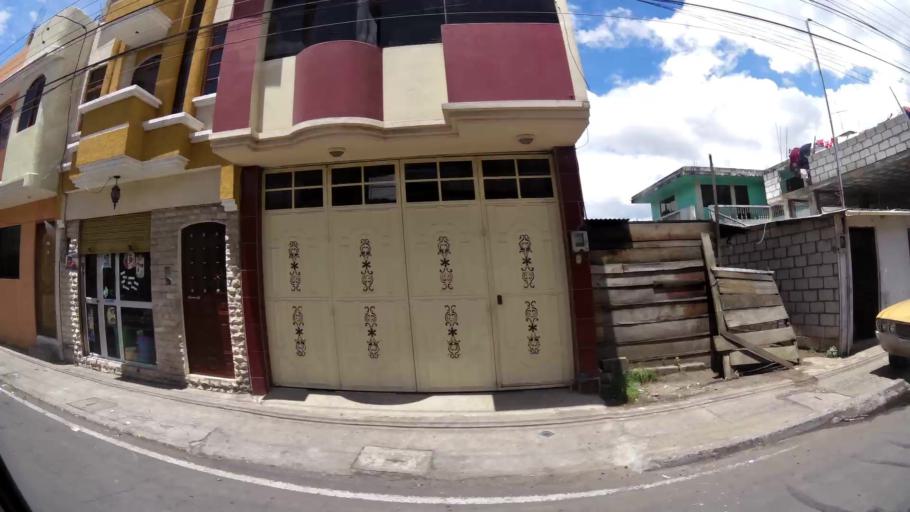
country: EC
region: Tungurahua
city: Pelileo
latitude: -1.3263
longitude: -78.5474
